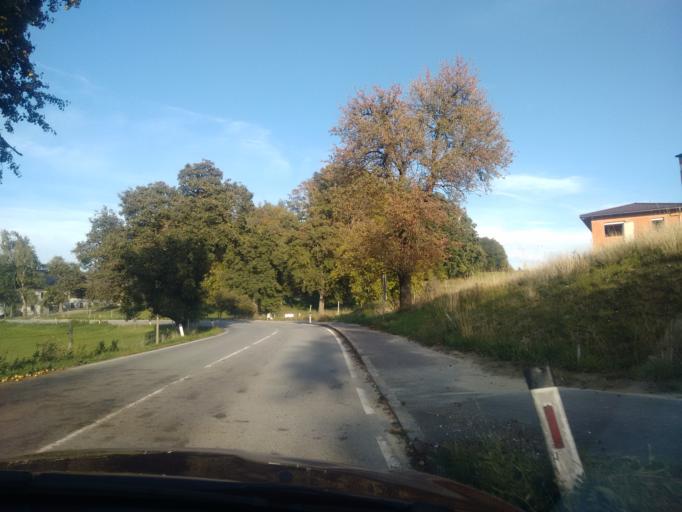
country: AT
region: Upper Austria
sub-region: Politischer Bezirk Vocklabruck
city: Wolfsegg am Hausruck
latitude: 48.0998
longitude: 13.6702
